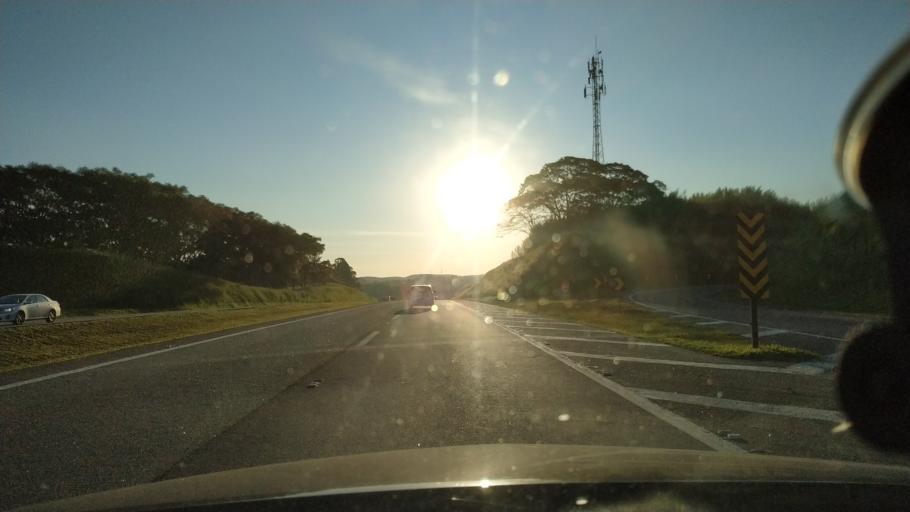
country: BR
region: Sao Paulo
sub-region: Sao Jose Dos Campos
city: Sao Jose dos Campos
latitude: -23.2677
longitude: -45.8224
